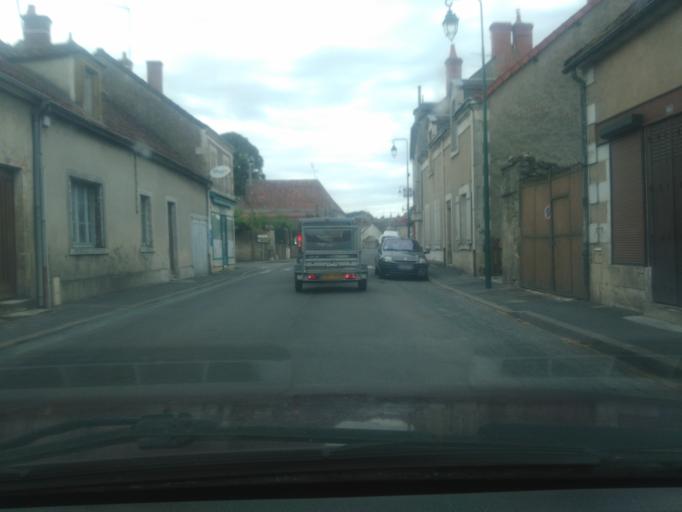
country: FR
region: Centre
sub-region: Departement du Cher
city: Charenton-du-Cher
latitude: 46.7306
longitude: 2.6396
